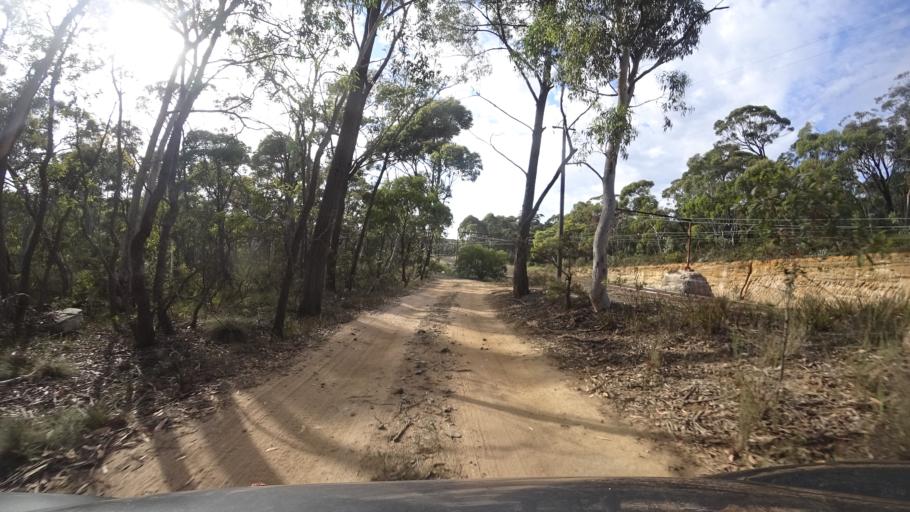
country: AU
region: New South Wales
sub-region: Lithgow
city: Lithgow
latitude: -33.4767
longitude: 150.2443
